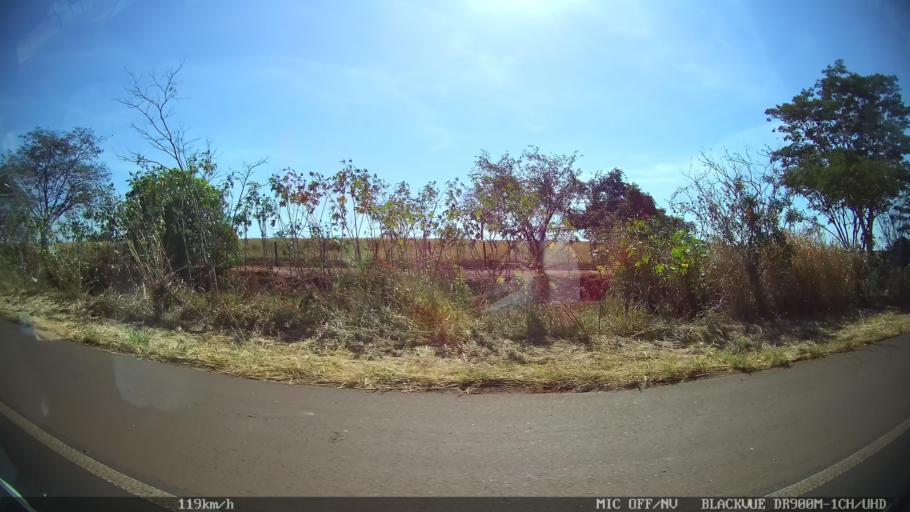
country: BR
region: Sao Paulo
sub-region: Barretos
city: Barretos
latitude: -20.4977
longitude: -48.5352
